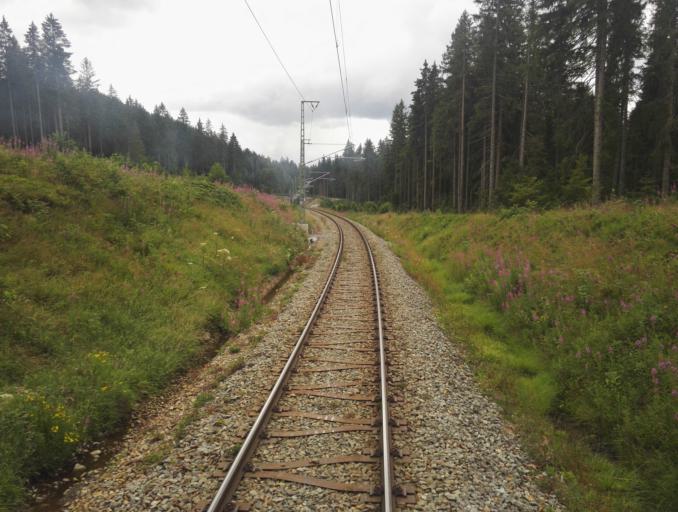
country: DE
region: Baden-Wuerttemberg
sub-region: Freiburg Region
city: Hinterzarten
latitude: 47.8470
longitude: 8.1270
